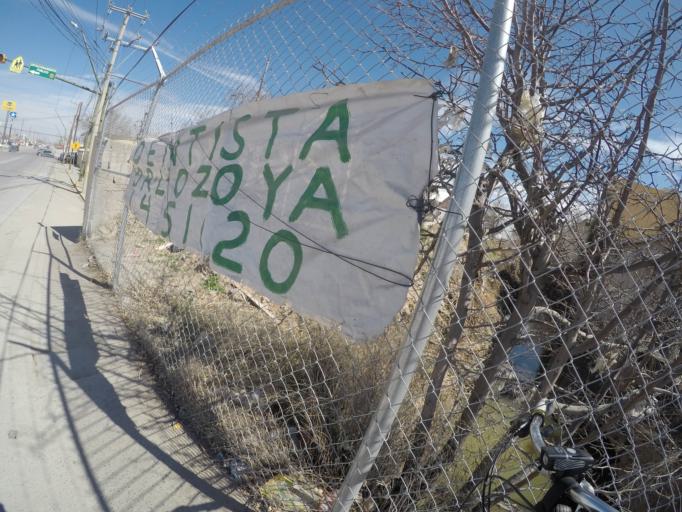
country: US
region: Texas
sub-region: El Paso County
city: Socorro
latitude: 31.6484
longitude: -106.3560
